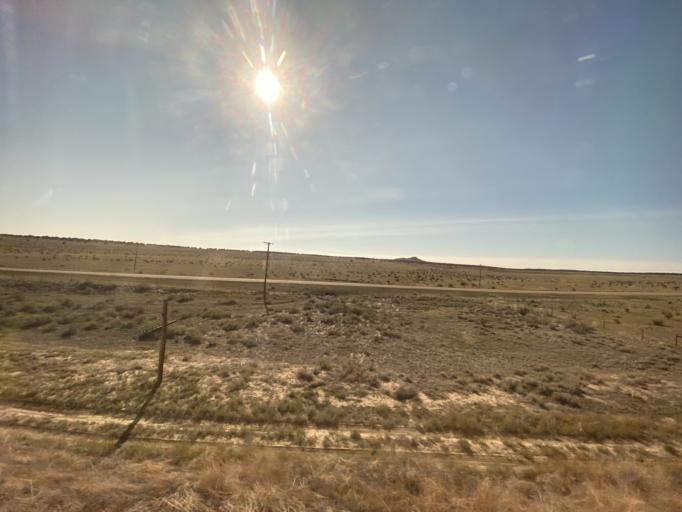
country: US
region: Colorado
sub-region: Otero County
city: Fowler
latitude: 37.5757
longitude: -104.0491
